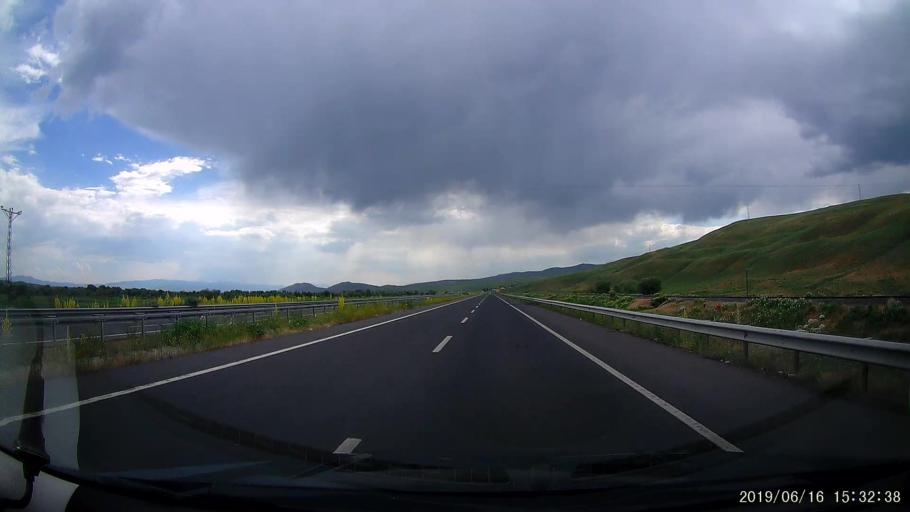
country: TR
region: Erzurum
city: Horasan
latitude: 40.0297
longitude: 42.0412
